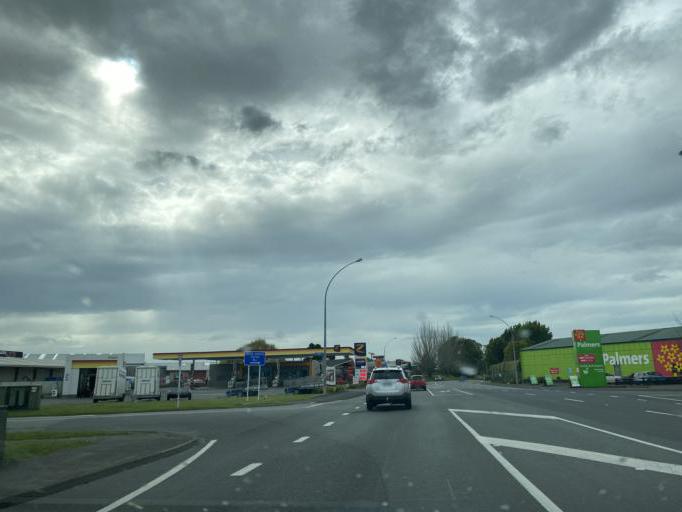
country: NZ
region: Waikato
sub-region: Hamilton City
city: Hamilton
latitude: -37.7867
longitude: 175.2568
